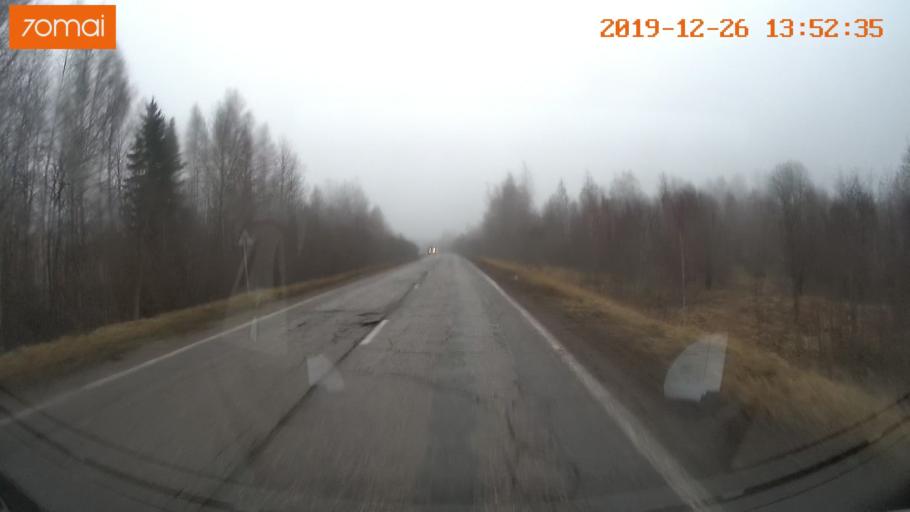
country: RU
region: Jaroslavl
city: Poshekhon'ye
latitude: 58.6299
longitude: 38.6030
